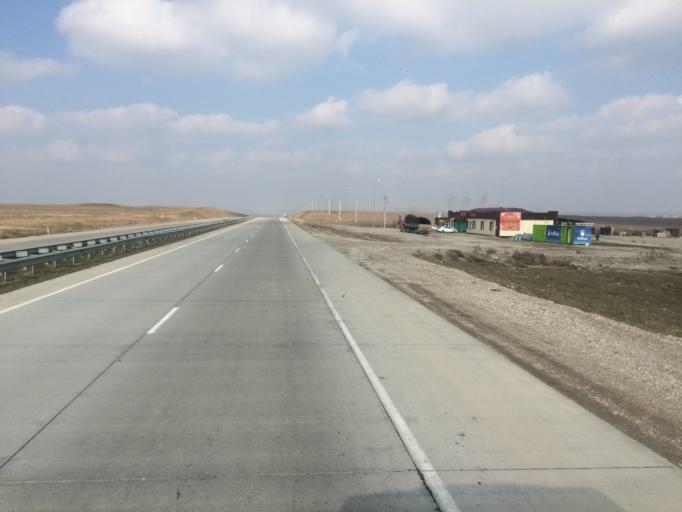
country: KZ
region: Ongtustik Qazaqstan
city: Temirlanovka
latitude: 42.5685
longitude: 69.3107
